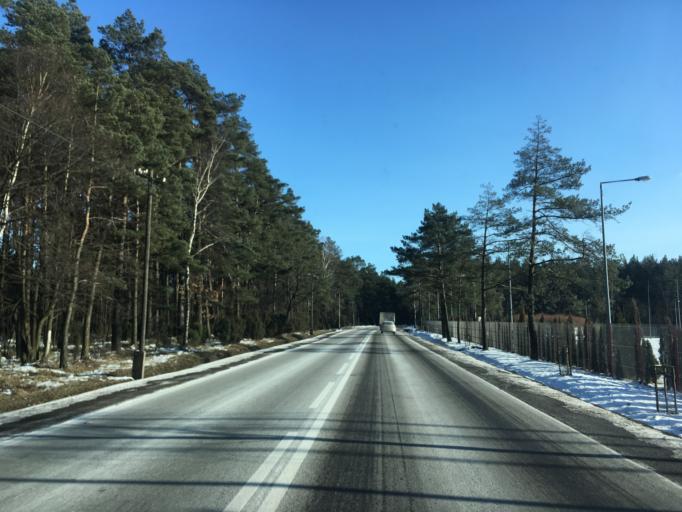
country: PL
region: Pomeranian Voivodeship
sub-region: Powiat koscierski
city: Lipusz
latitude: 54.1255
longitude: 17.8775
